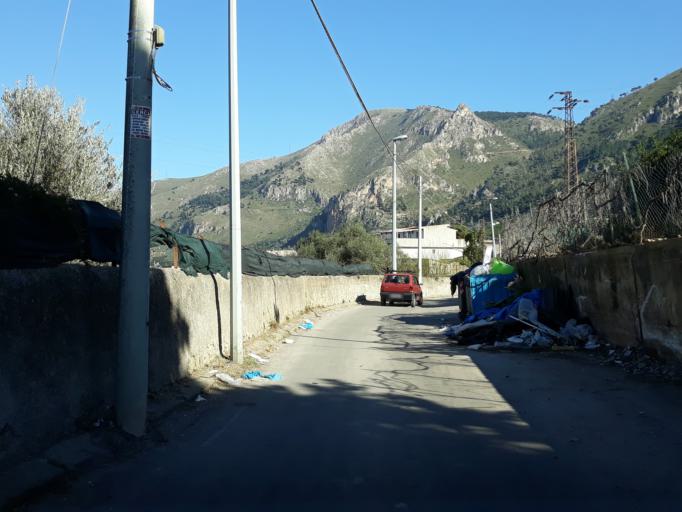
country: IT
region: Sicily
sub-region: Palermo
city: Villa Ciambra
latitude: 38.0758
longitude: 13.3521
